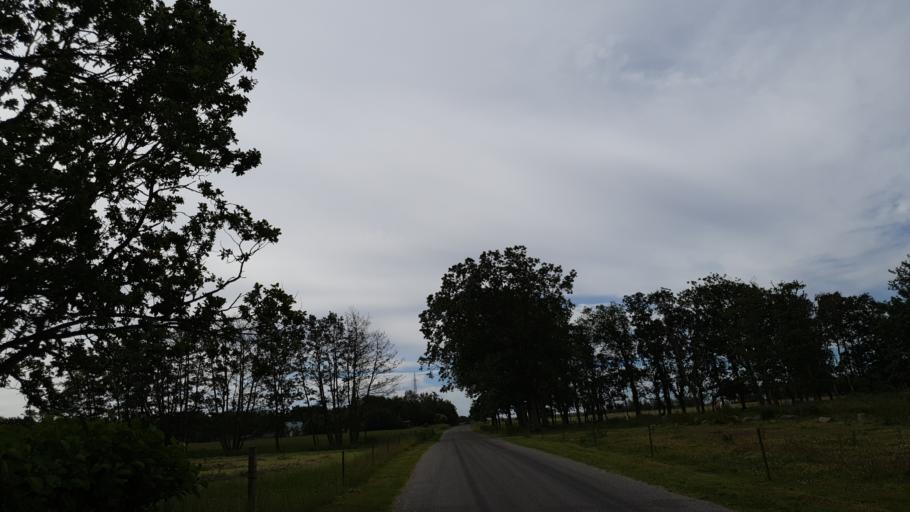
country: DK
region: North Denmark
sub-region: Laeso Kommune
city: Byrum
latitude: 57.2481
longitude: 10.9848
